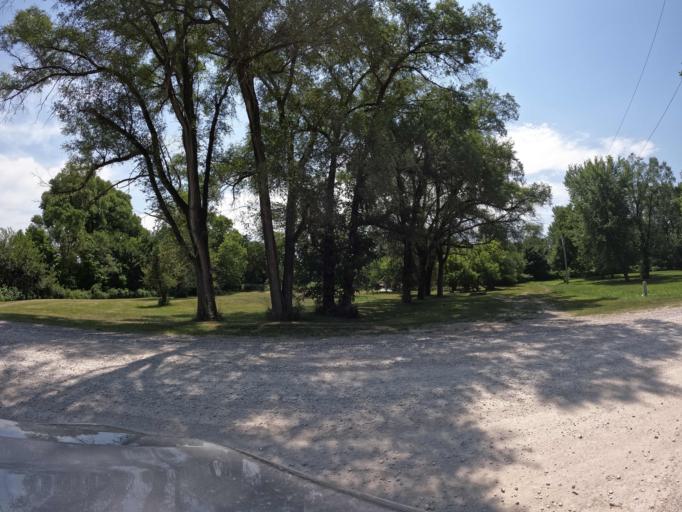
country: US
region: Iowa
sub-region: Appanoose County
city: Centerville
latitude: 40.7769
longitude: -92.9483
